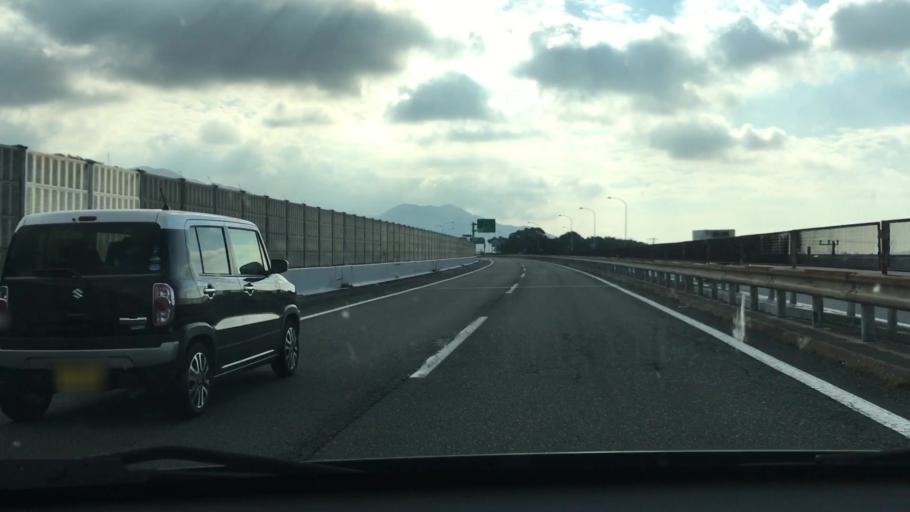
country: JP
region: Kumamoto
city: Yatsushiro
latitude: 32.5166
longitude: 130.6503
